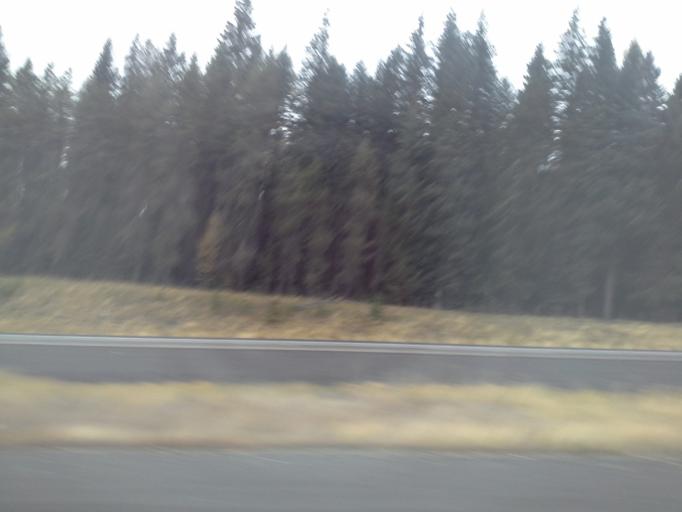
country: US
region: Oregon
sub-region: Umatilla County
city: Mission
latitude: 45.5174
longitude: -118.4357
